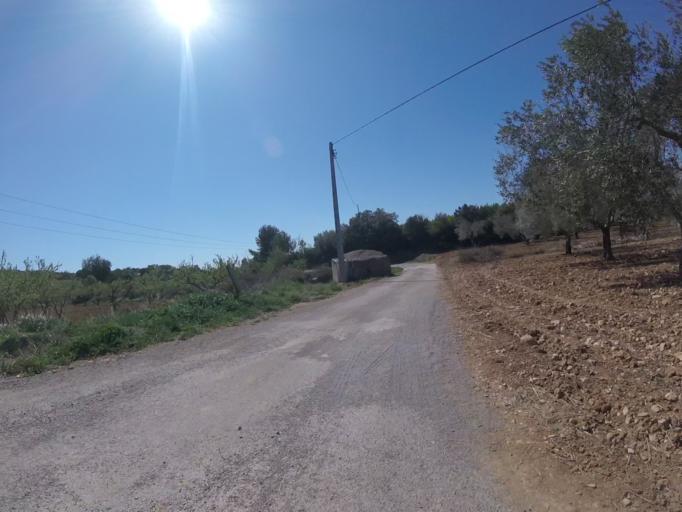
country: ES
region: Valencia
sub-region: Provincia de Castello
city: Cuevas de Vinroma
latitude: 40.3741
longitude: 0.1346
